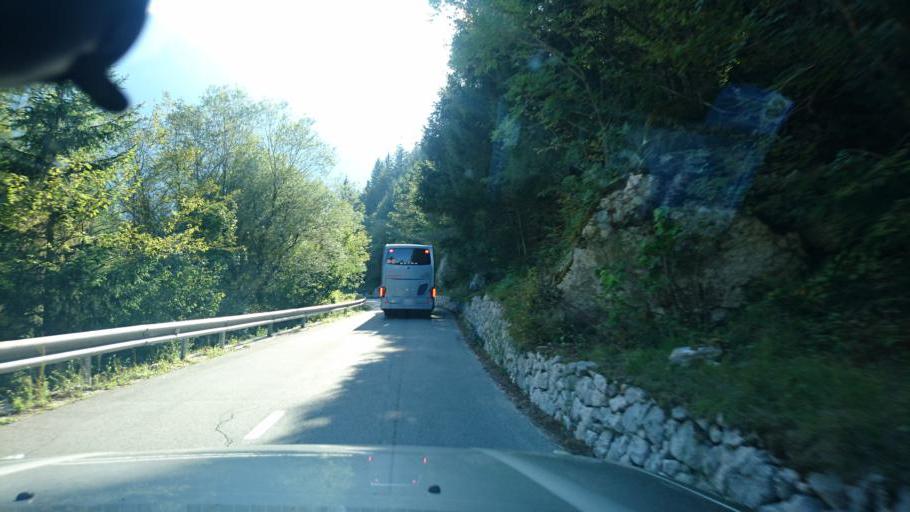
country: SI
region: Bovec
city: Bovec
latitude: 46.3407
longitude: 13.6495
